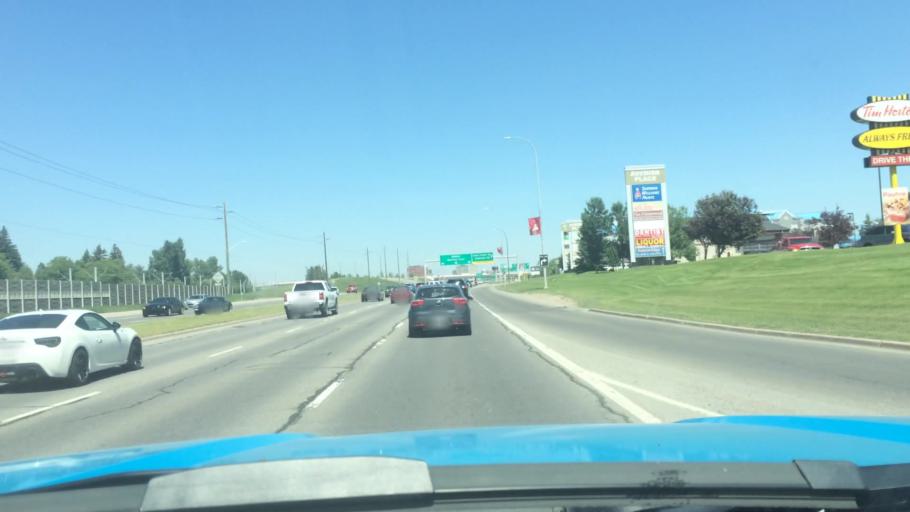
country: CA
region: Alberta
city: Calgary
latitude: 50.9437
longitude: -114.0702
